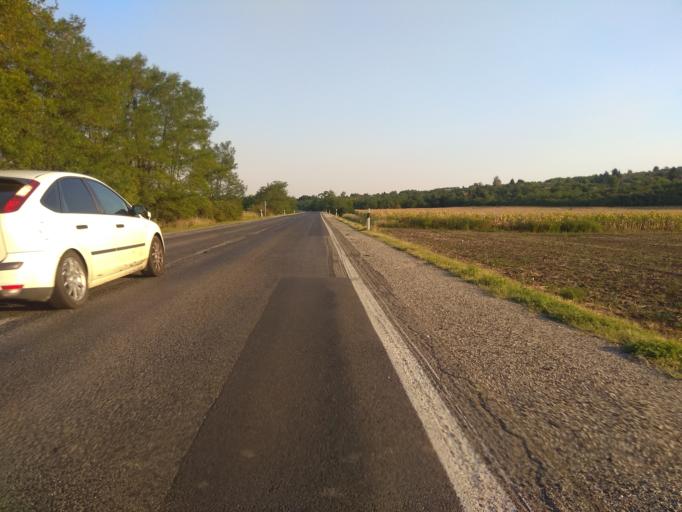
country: HU
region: Borsod-Abauj-Zemplen
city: Nyekladhaza
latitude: 47.9722
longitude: 20.8306
